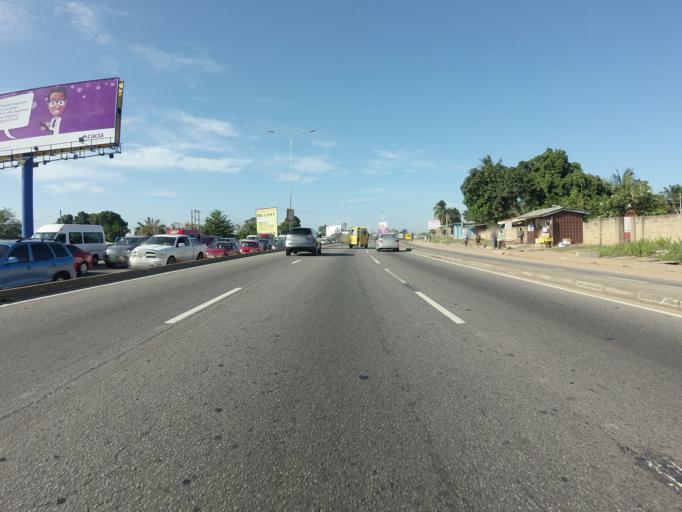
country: GH
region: Greater Accra
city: Gbawe
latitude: 5.5616
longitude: -0.2907
